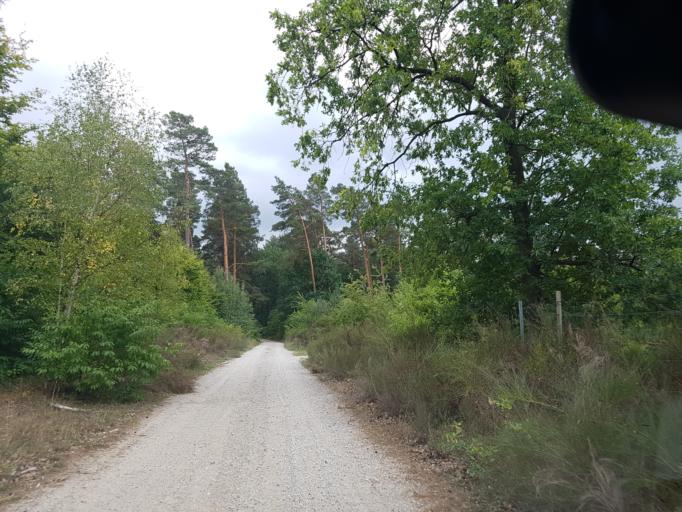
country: DE
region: Saxony-Anhalt
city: Rosslau
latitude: 52.0204
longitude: 12.2920
